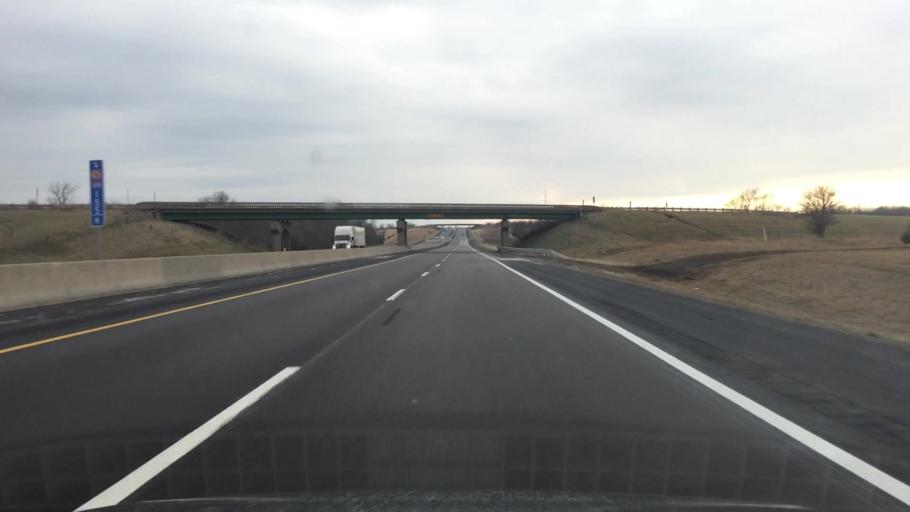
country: US
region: Kansas
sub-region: Osage County
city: Osage City
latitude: 38.7546
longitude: -95.9383
